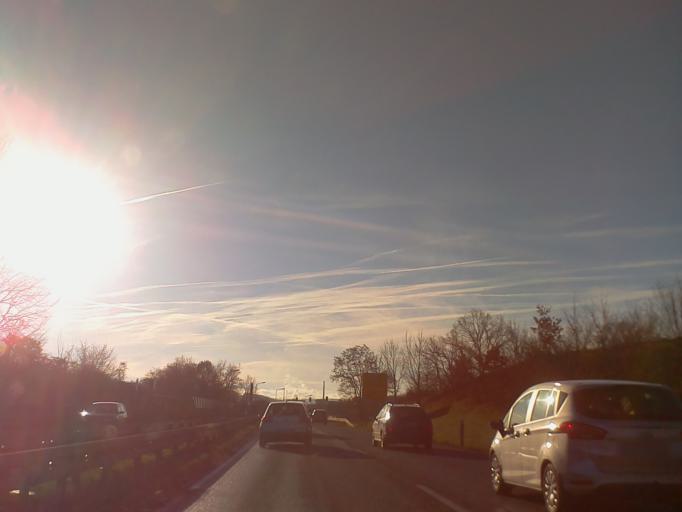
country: DE
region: Thuringia
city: Rudolstadt
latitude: 50.7110
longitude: 11.3172
